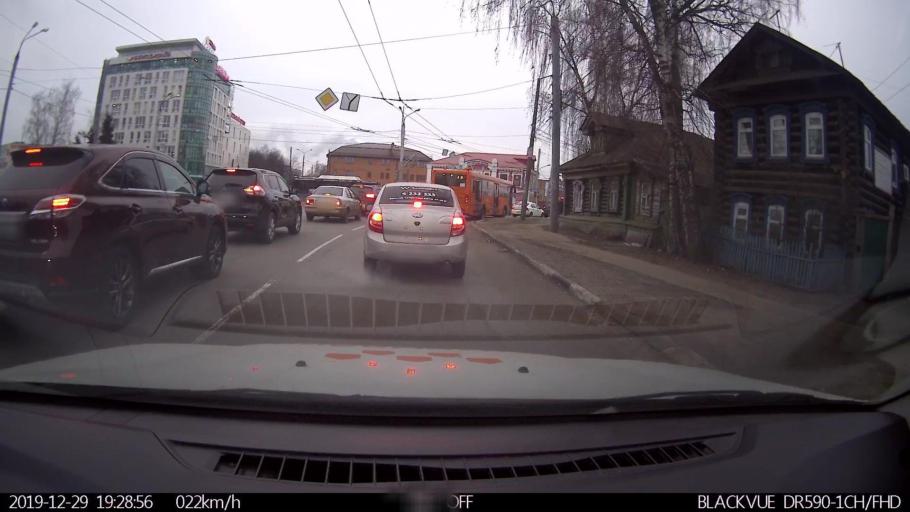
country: RU
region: Nizjnij Novgorod
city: Neklyudovo
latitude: 56.3617
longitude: 43.8616
